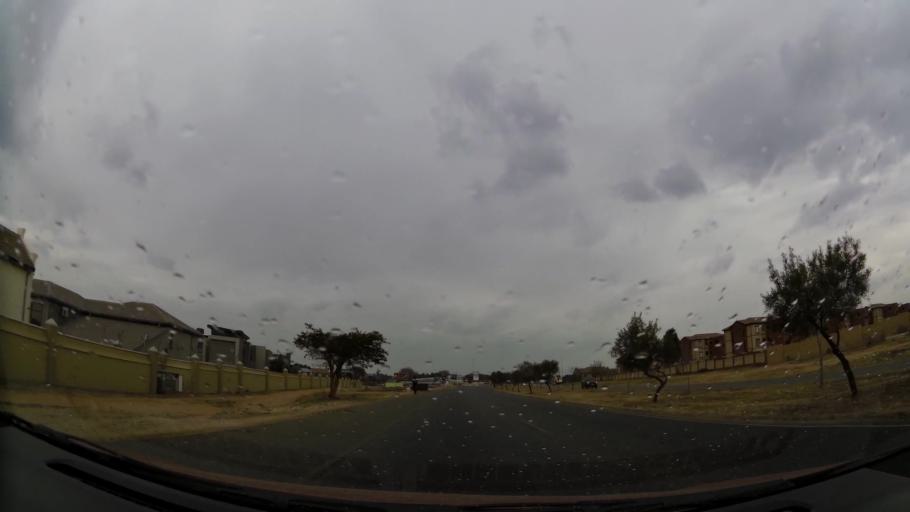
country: ZA
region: Gauteng
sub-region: City of Johannesburg Metropolitan Municipality
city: Roodepoort
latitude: -26.0919
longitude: 27.9270
